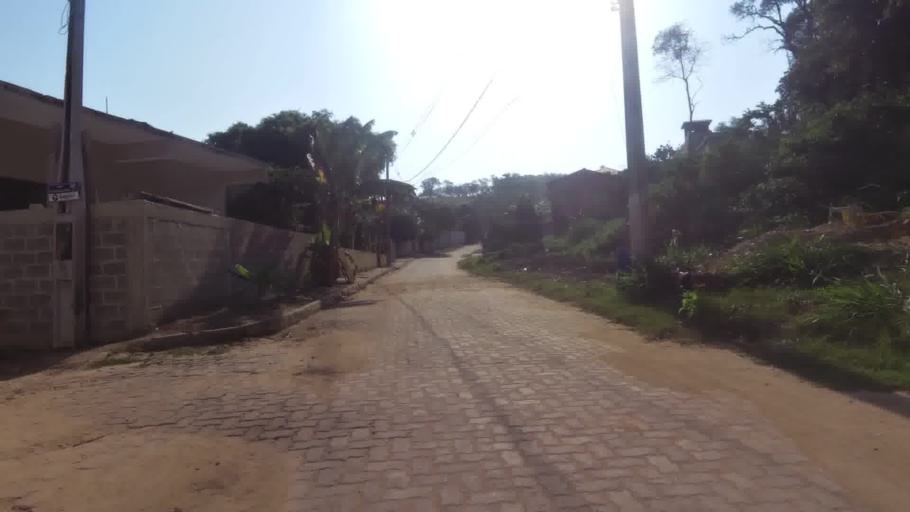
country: BR
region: Espirito Santo
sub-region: Piuma
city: Piuma
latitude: -20.8608
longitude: -40.7590
